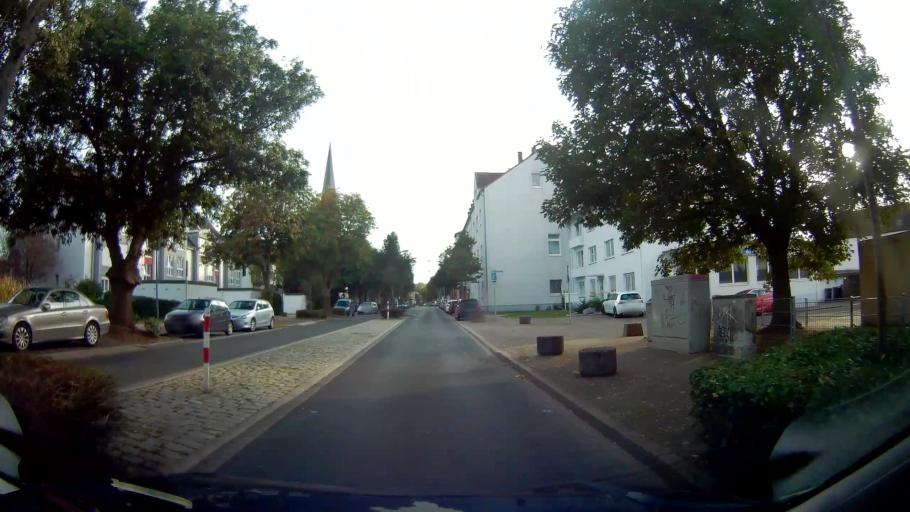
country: DE
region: North Rhine-Westphalia
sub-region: Regierungsbezirk Arnsberg
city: Herne
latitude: 51.5456
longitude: 7.2608
